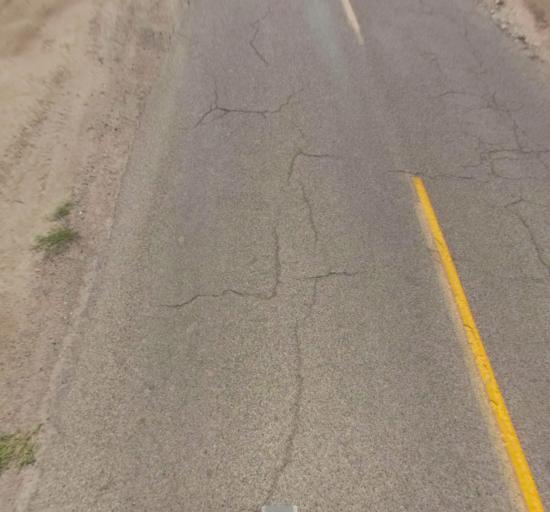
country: US
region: California
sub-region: Fresno County
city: Kerman
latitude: 36.8366
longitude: -120.2055
